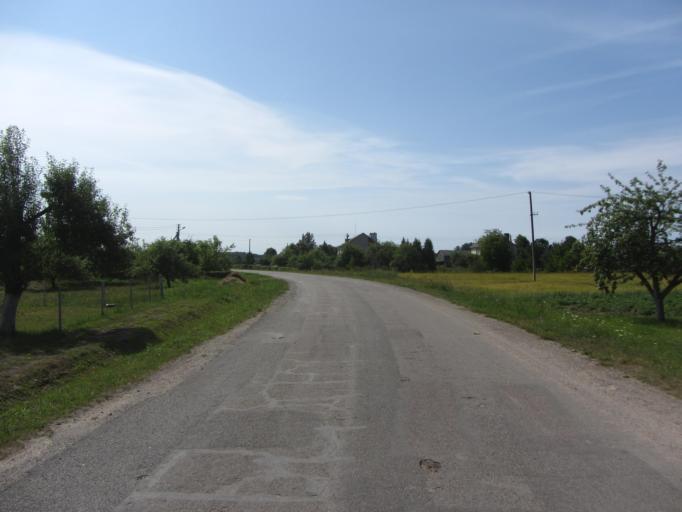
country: LT
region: Alytaus apskritis
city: Druskininkai
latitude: 54.0997
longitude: 24.1067
